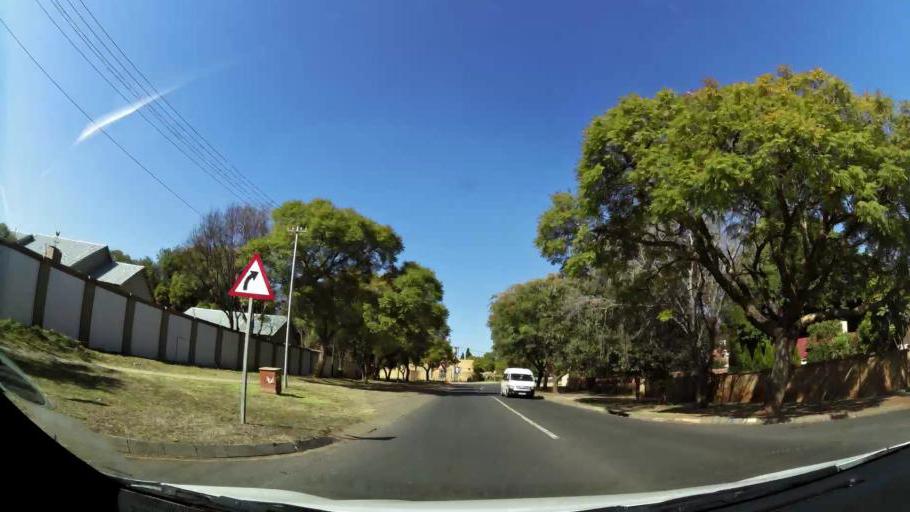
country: ZA
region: Gauteng
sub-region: City of Tshwane Metropolitan Municipality
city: Pretoria
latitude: -25.7880
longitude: 28.2389
